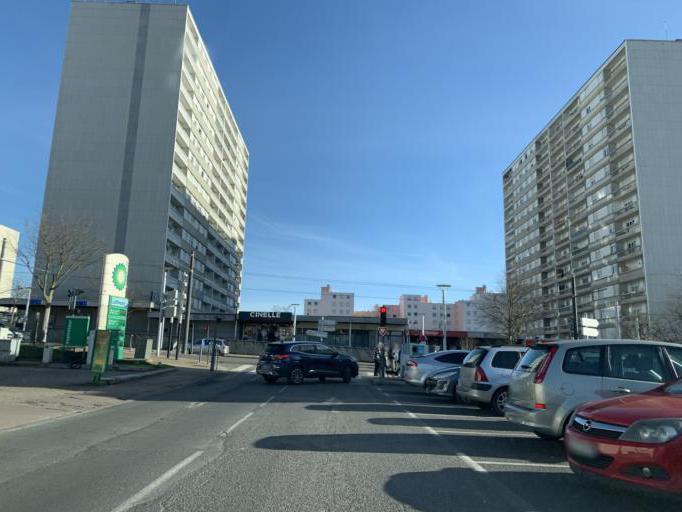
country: FR
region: Rhone-Alpes
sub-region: Departement du Rhone
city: Rillieux-la-Pape
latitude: 45.8177
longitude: 4.9007
